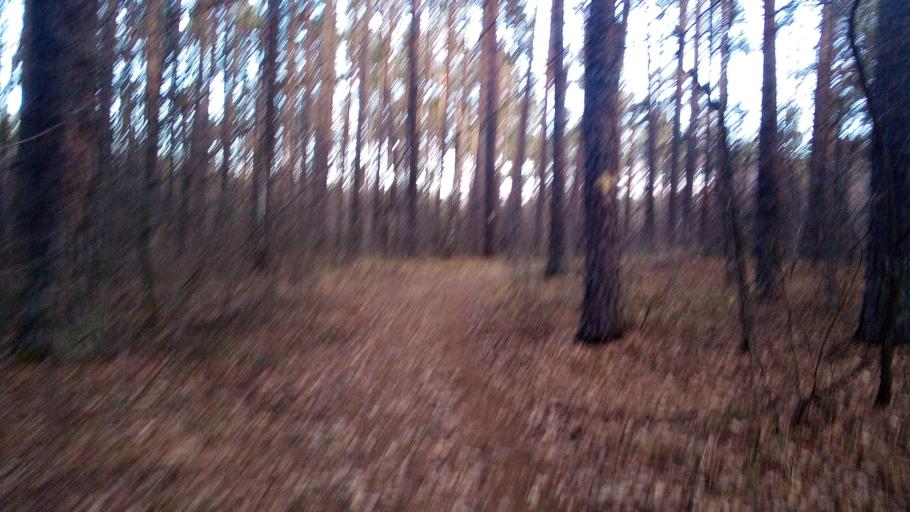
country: RU
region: Chelyabinsk
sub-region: Gorod Chelyabinsk
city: Chelyabinsk
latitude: 55.1592
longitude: 61.3445
